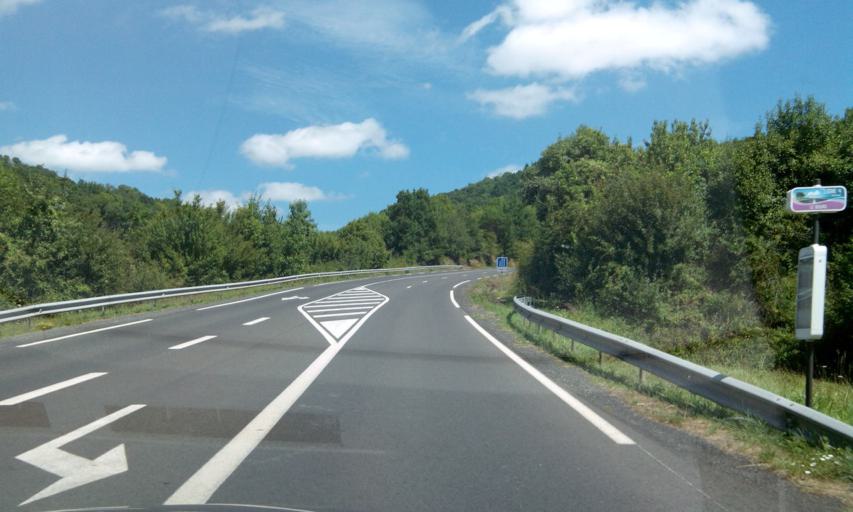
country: FR
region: Limousin
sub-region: Departement de la Correze
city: Meyssac
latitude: 45.0716
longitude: 1.6197
